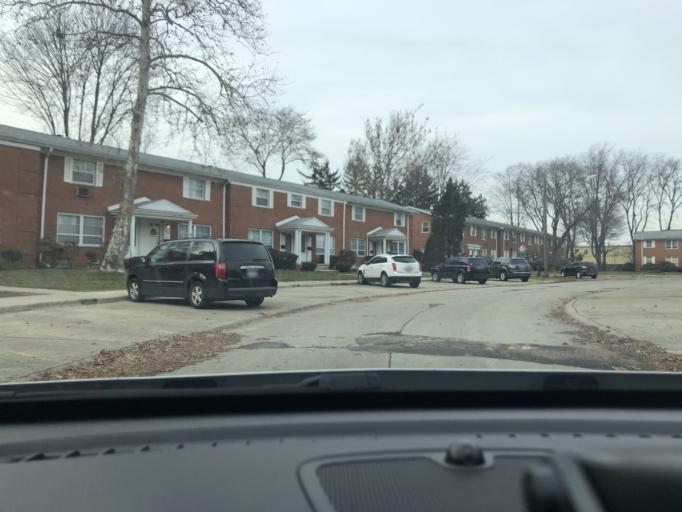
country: US
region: Michigan
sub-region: Wayne County
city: Dearborn Heights
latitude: 42.3404
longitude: -83.2410
